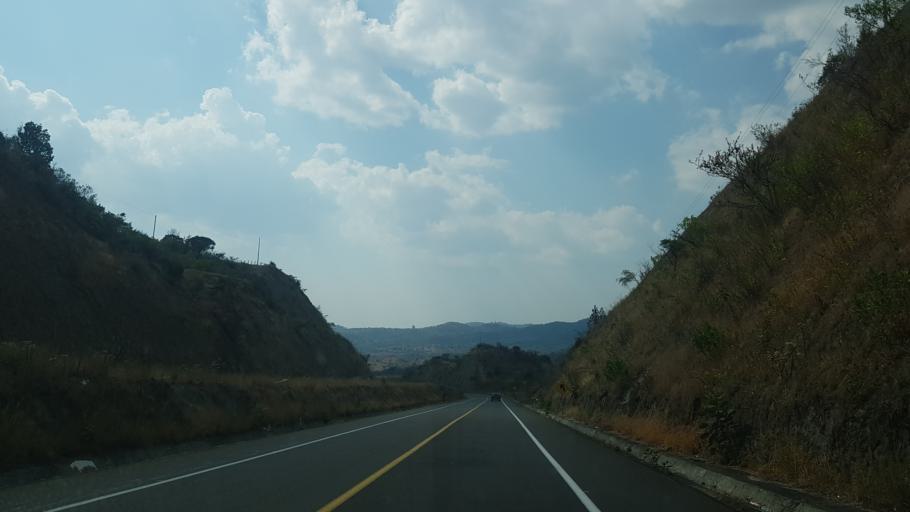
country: MX
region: Puebla
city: San Juan Amecac
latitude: 18.8198
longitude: -98.6829
